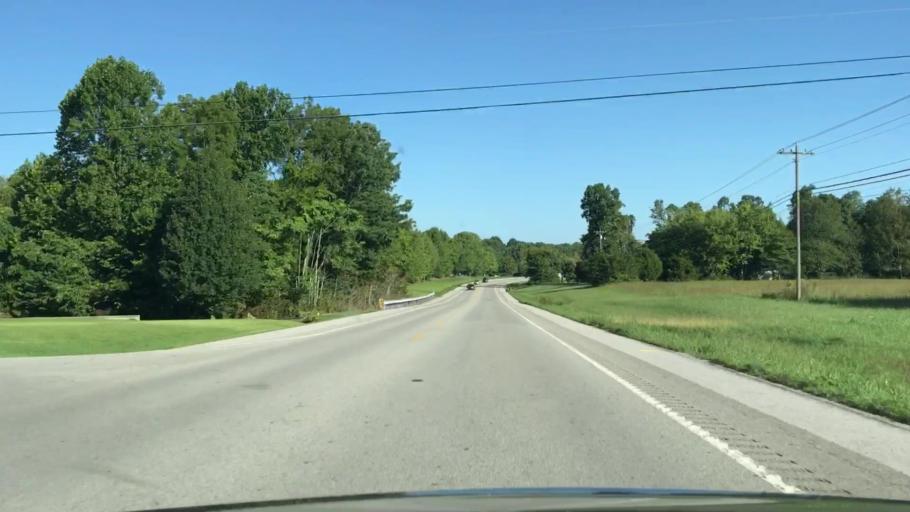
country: US
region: Tennessee
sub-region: Jackson County
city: Dodson Branch
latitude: 36.2673
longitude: -85.6153
